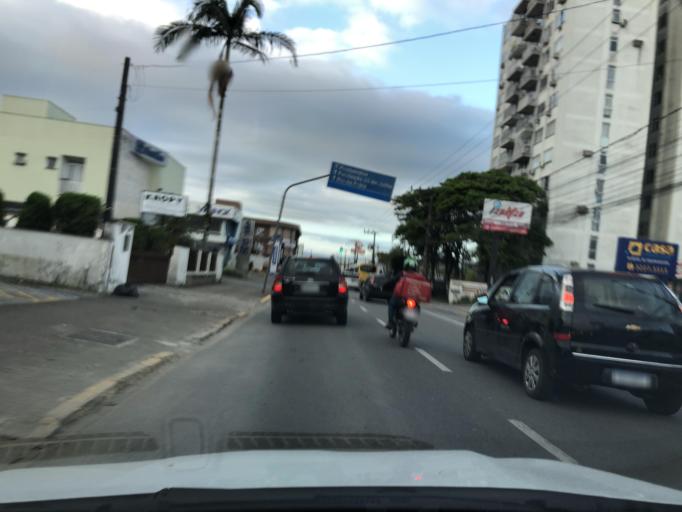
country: BR
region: Santa Catarina
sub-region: Joinville
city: Joinville
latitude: -26.2833
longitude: -48.8493
